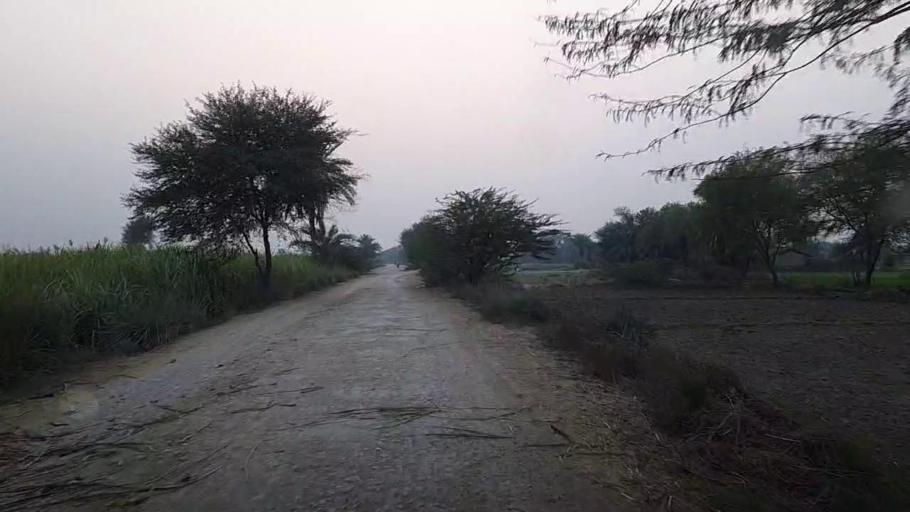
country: PK
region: Sindh
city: Kandiari
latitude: 26.9784
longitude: 68.4867
